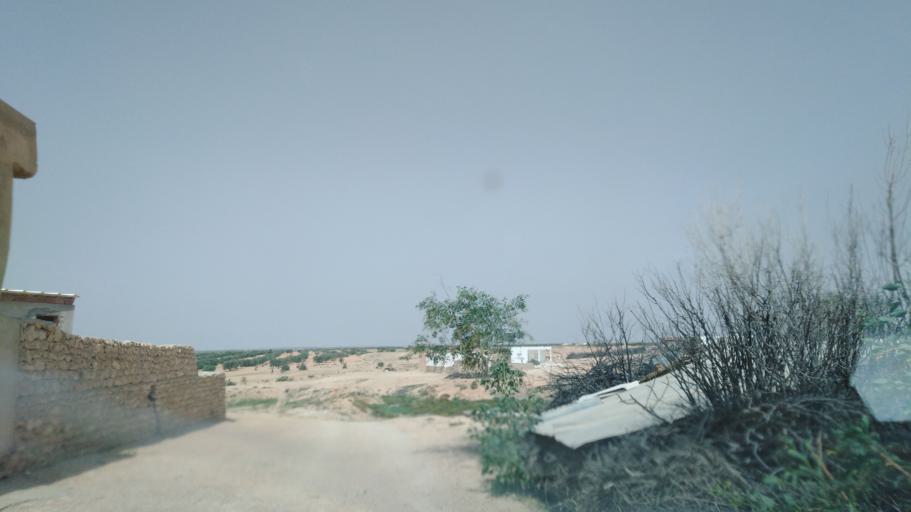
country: TN
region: Safaqis
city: Sfax
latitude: 34.6385
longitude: 10.5693
